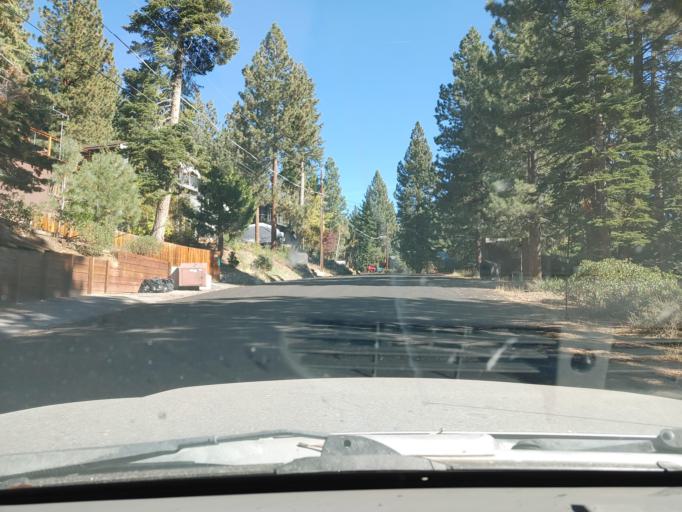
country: US
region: California
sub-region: Placer County
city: Kings Beach
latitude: 39.2563
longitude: -120.0321
